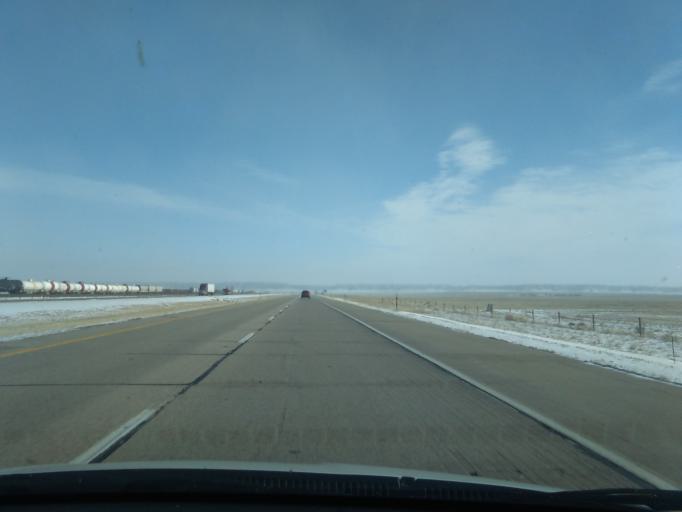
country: US
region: Wyoming
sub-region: Laramie County
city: Pine Bluffs
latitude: 41.1485
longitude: -104.1411
